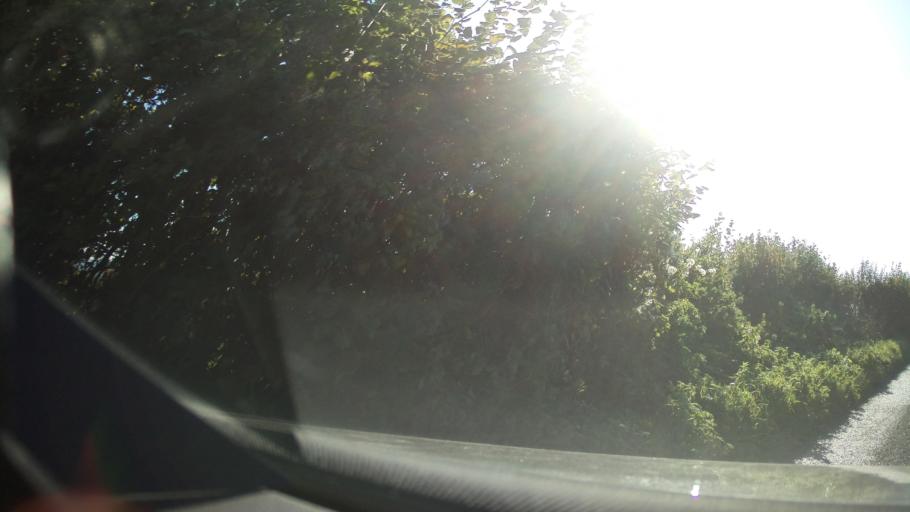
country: GB
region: England
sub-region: Somerset
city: Bruton
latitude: 51.1512
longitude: -2.4210
